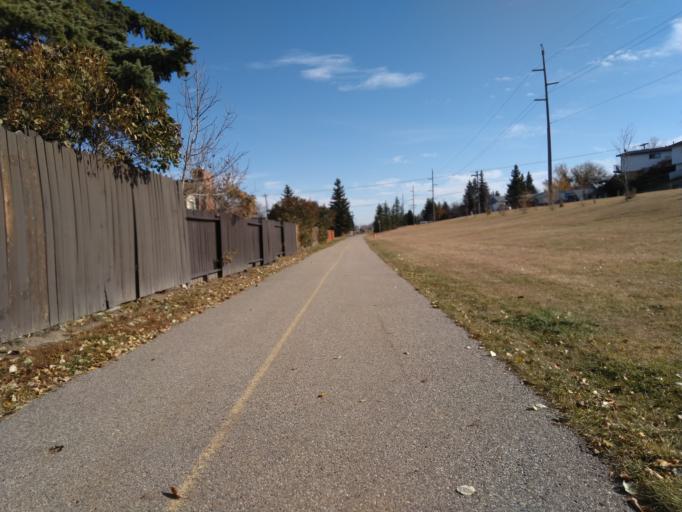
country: CA
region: Alberta
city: Calgary
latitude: 51.1252
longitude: -114.0877
